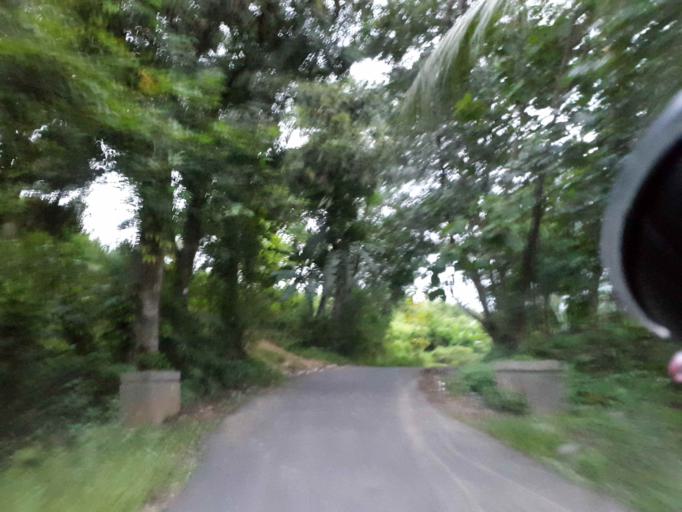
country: ID
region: Central Java
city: Randudongkal
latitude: -7.0727
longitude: 109.3309
